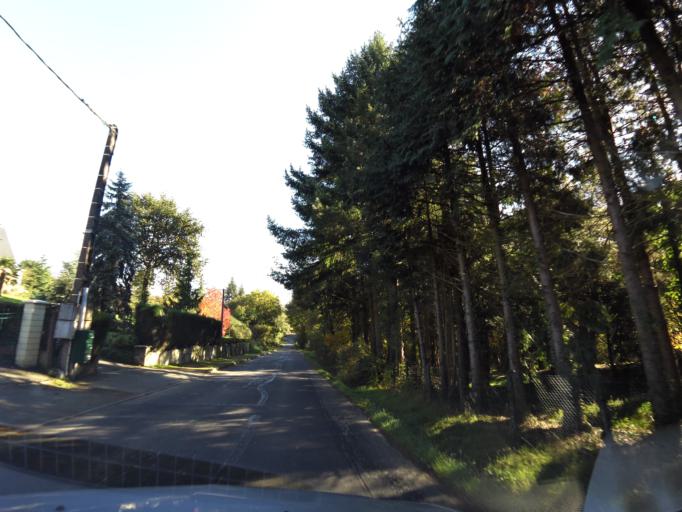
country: FR
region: Brittany
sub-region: Departement d'Ille-et-Vilaine
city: Pance
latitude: 47.8752
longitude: -1.6843
